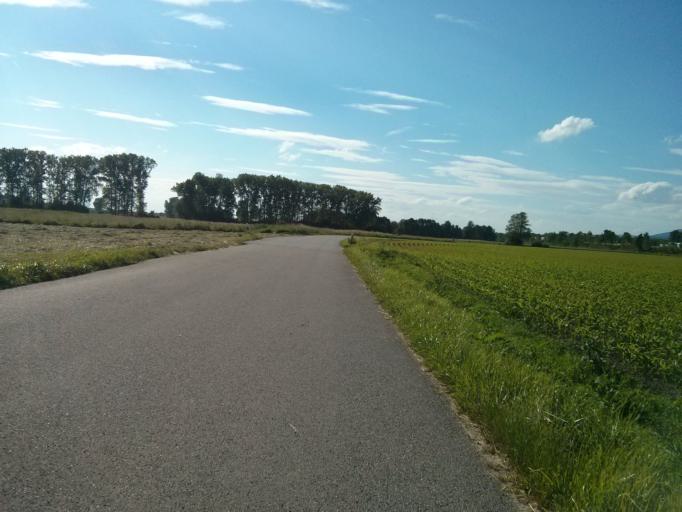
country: DE
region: Bavaria
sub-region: Lower Bavaria
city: Metten
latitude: 48.8297
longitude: 12.9092
